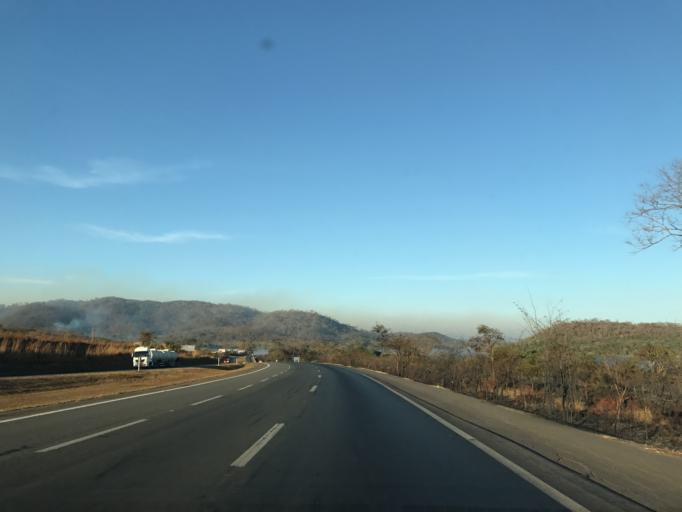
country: BR
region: Goias
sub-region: Goianapolis
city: Goianapolis
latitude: -16.5077
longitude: -49.1166
